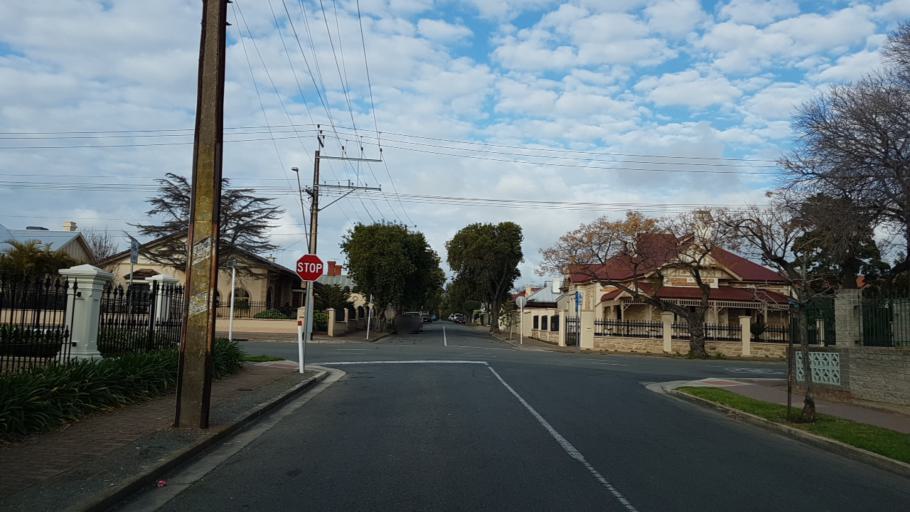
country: AU
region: South Australia
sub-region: Adelaide
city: North Adelaide
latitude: -34.8951
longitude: 138.5897
